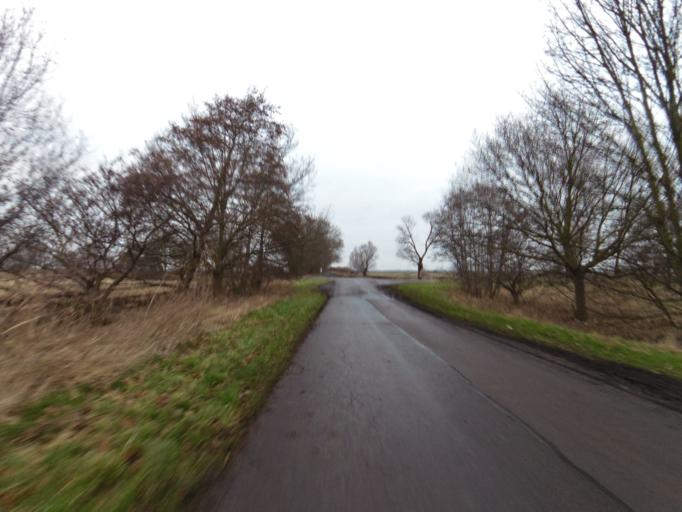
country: GB
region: England
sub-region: Cambridgeshire
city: Bottisham
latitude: 52.2764
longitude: 0.2651
